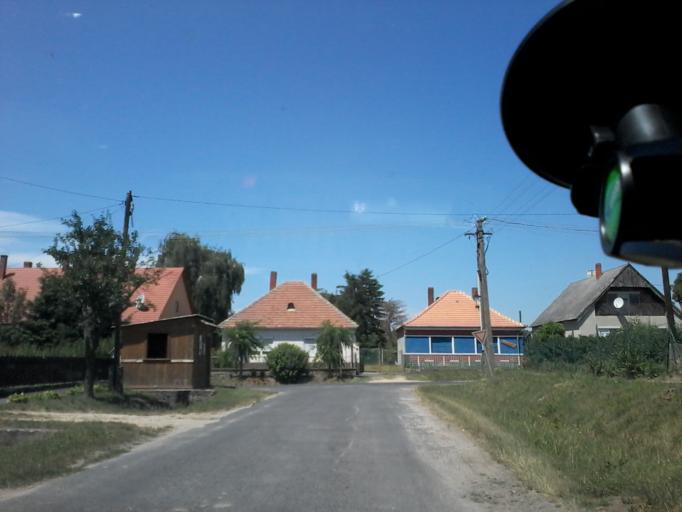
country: HU
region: Vas
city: Janoshaza
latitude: 47.1664
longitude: 17.1156
